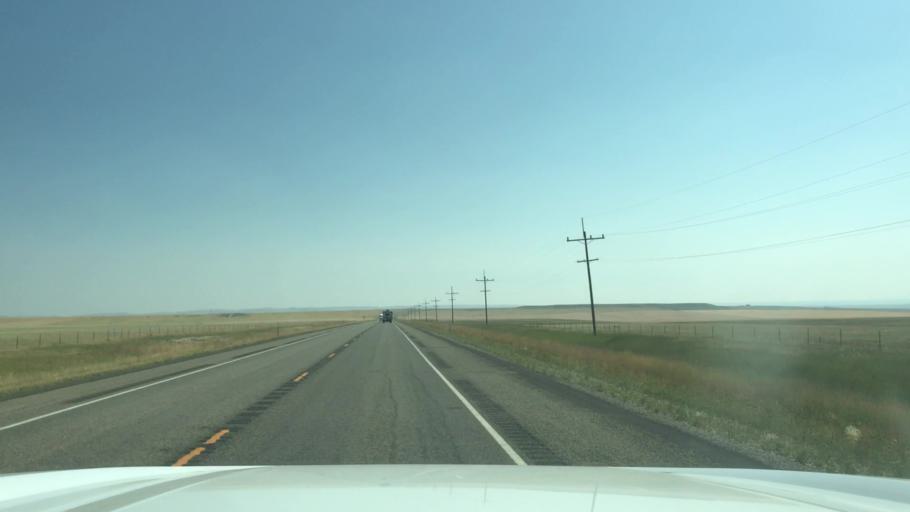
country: US
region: Montana
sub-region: Wheatland County
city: Harlowton
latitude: 46.5007
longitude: -109.7661
